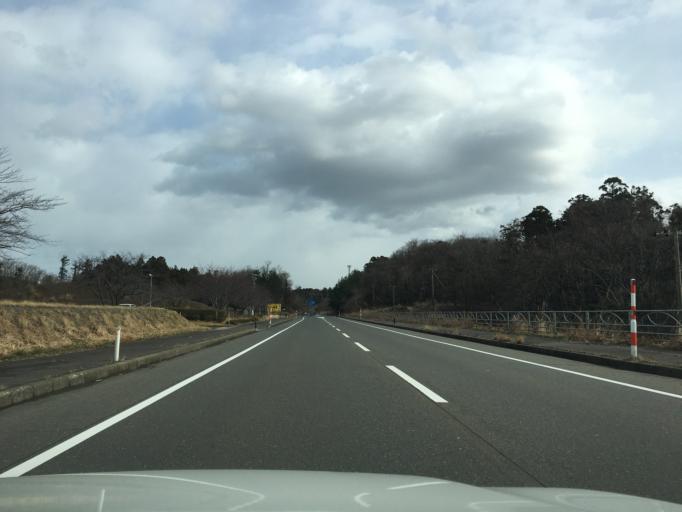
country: JP
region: Yamagata
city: Yuza
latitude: 39.2474
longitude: 139.9237
